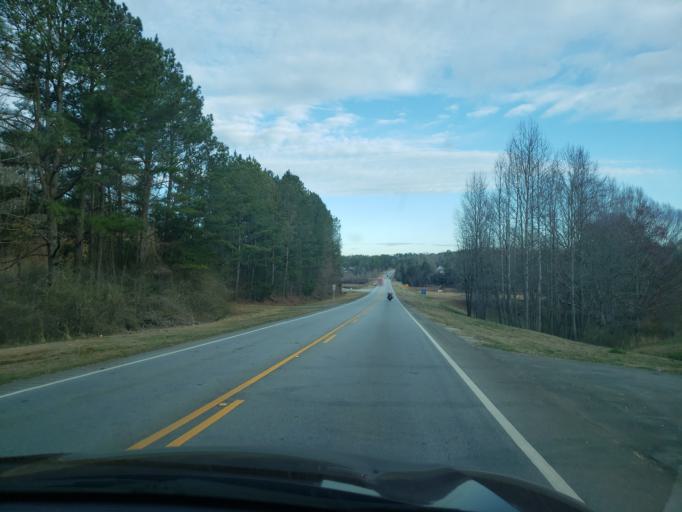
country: US
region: Alabama
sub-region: Randolph County
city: Wedowee
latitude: 33.3225
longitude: -85.4859
